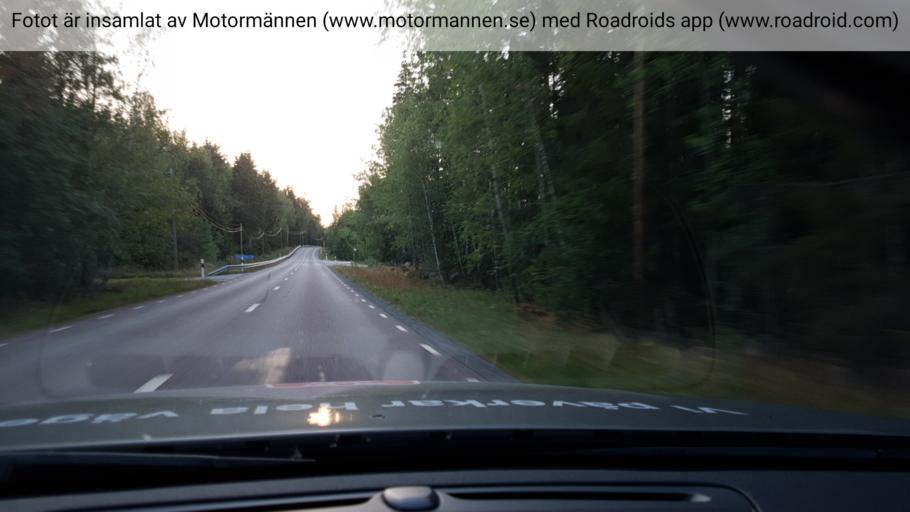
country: SE
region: Uppsala
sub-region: Heby Kommun
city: OEstervala
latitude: 60.0128
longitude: 17.2910
